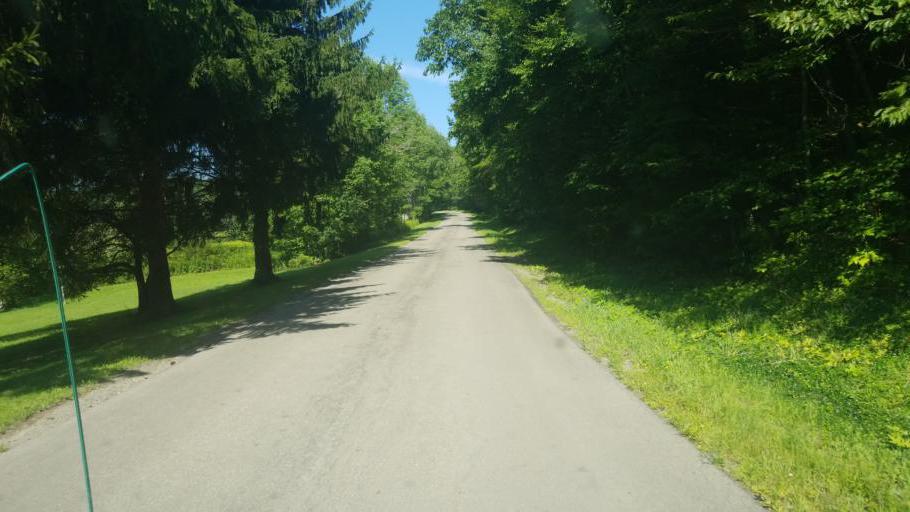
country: US
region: New York
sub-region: Allegany County
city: Wellsville
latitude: 42.0683
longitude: -78.0174
